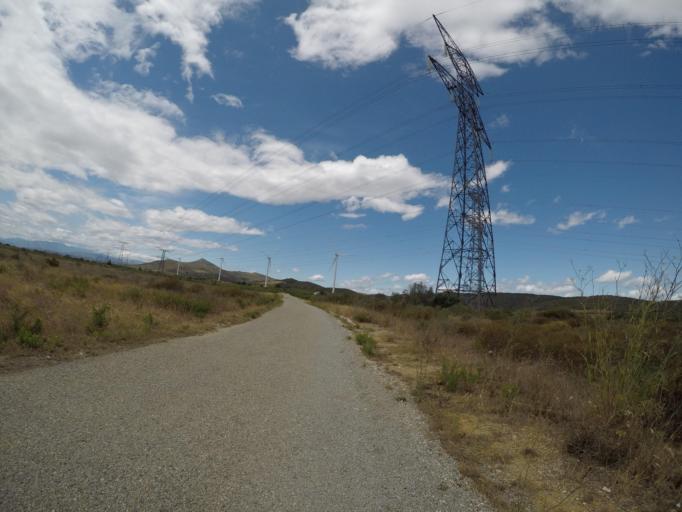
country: FR
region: Languedoc-Roussillon
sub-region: Departement des Pyrenees-Orientales
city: Pezilla-la-Riviere
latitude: 42.7208
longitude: 2.7563
